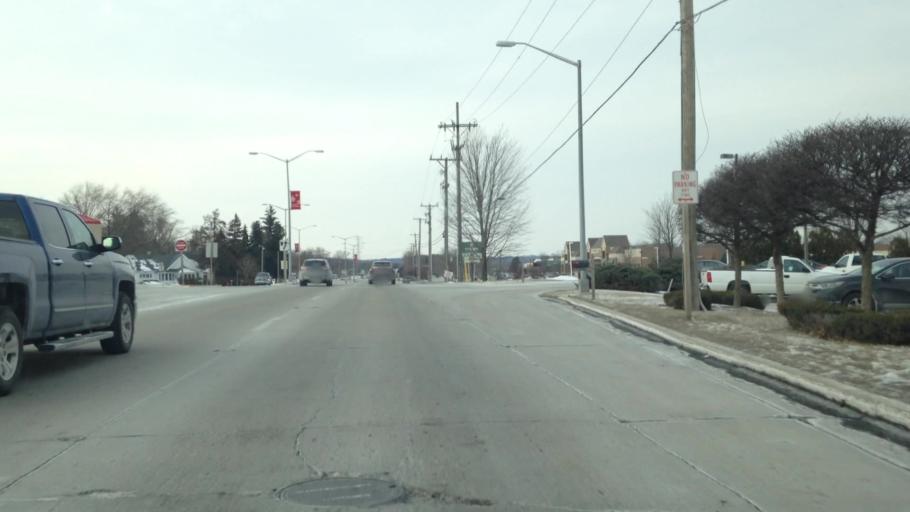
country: US
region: Wisconsin
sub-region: Waukesha County
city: Menomonee Falls
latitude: 43.1927
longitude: -88.1373
